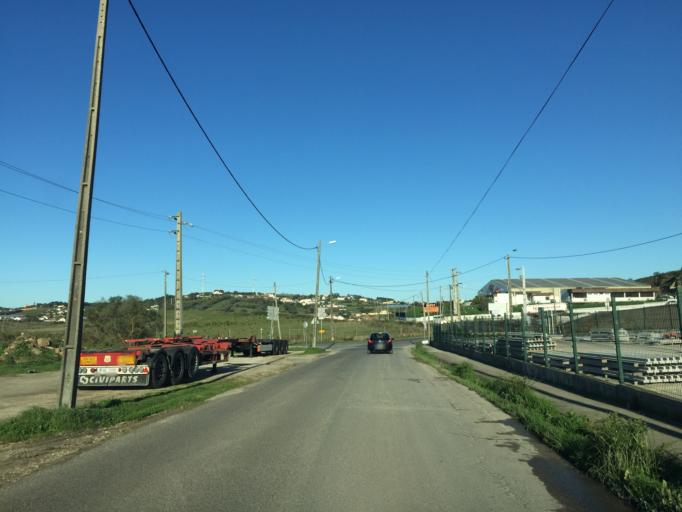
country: PT
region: Lisbon
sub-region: Odivelas
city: Canecas
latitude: 38.8270
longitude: -9.2467
